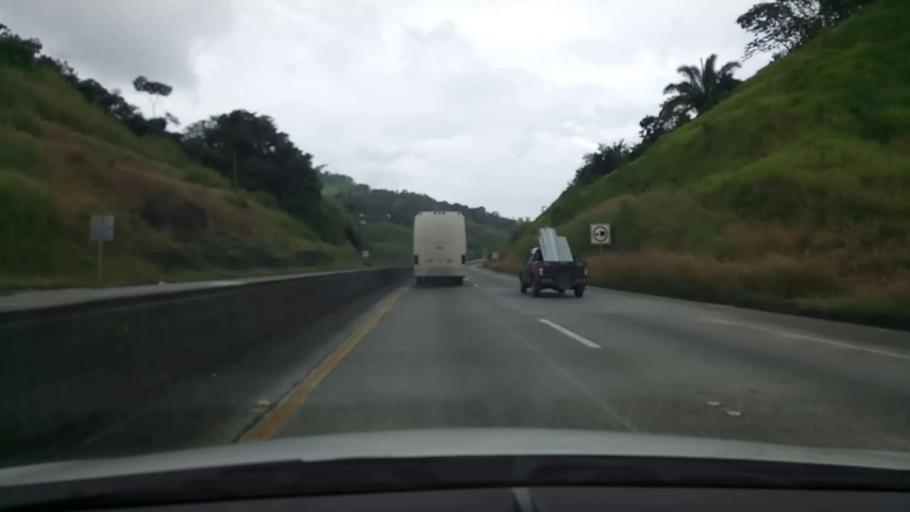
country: PA
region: Colon
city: Gatun
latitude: 9.2823
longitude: -79.7506
